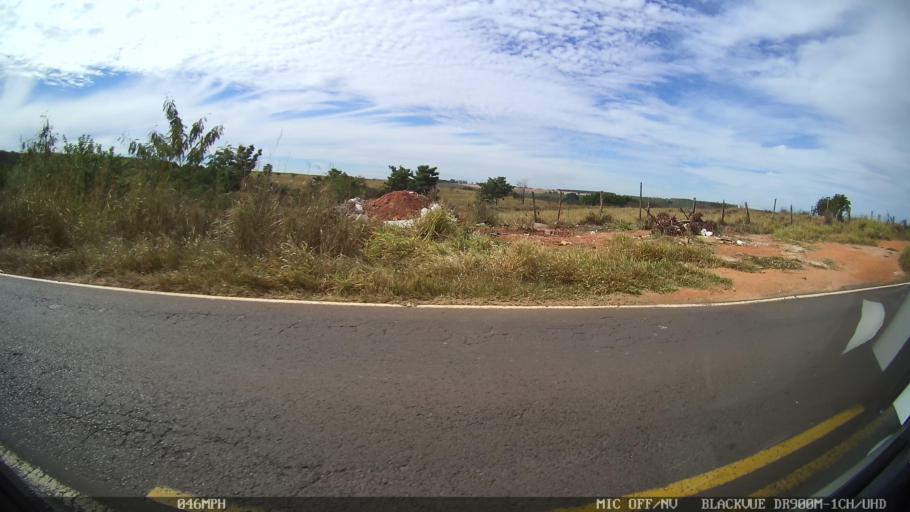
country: BR
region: Sao Paulo
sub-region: Catanduva
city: Catanduva
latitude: -21.1717
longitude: -48.9619
